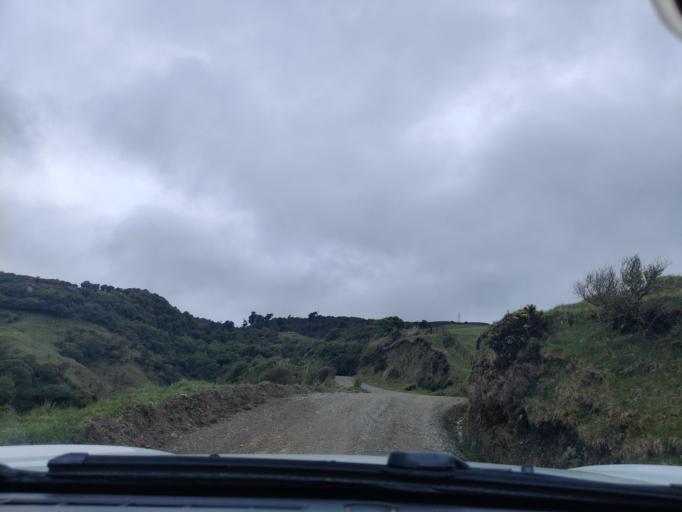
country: NZ
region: Manawatu-Wanganui
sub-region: Palmerston North City
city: Palmerston North
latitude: -40.2745
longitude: 175.8494
